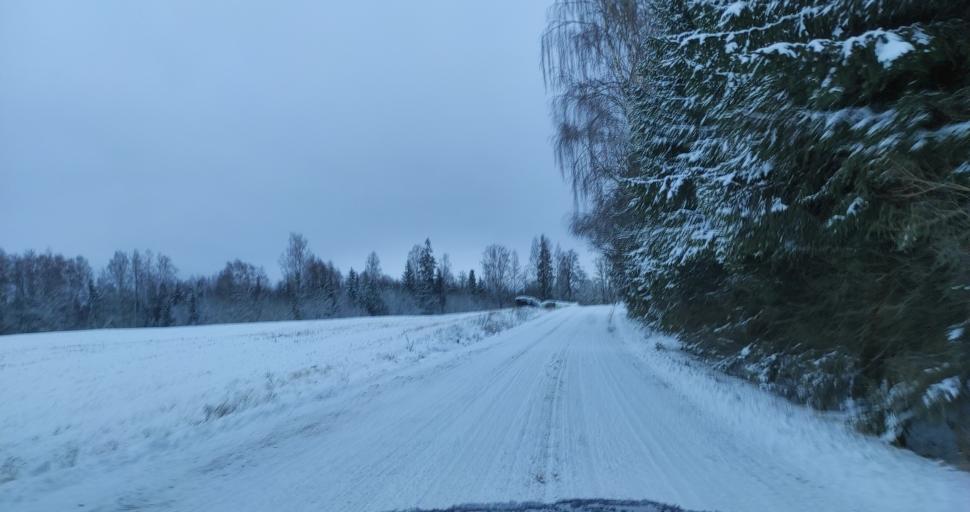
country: LV
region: Kuldigas Rajons
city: Kuldiga
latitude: 56.9507
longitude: 21.7707
